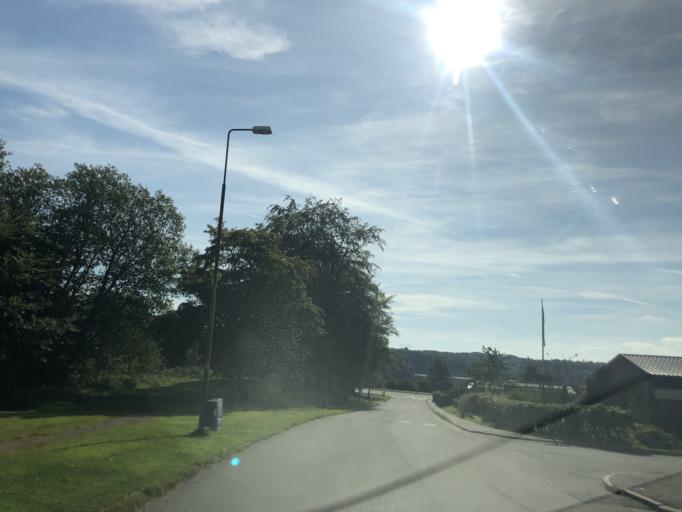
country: SE
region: Vaestra Goetaland
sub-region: Molndal
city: Moelndal
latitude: 57.6650
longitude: 12.0468
